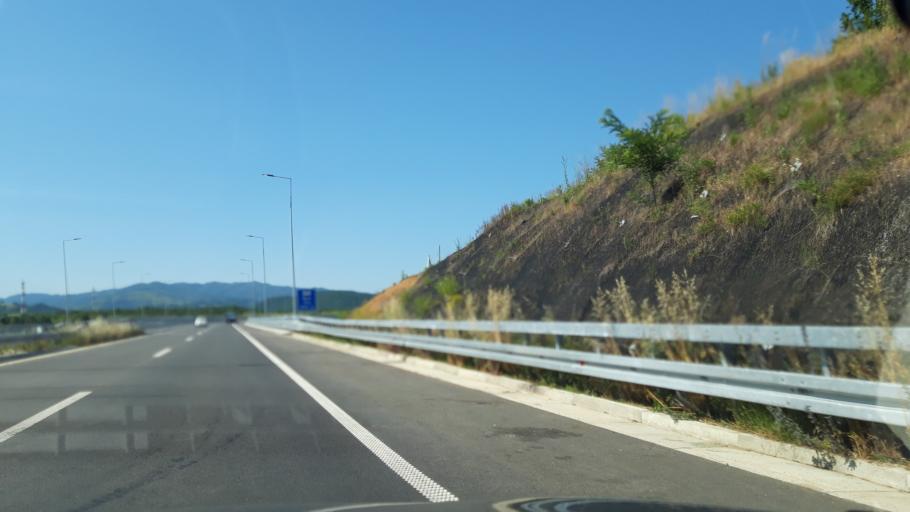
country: RS
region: Central Serbia
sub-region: Pcinjski Okrug
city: Vladicin Han
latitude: 42.7067
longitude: 22.0733
